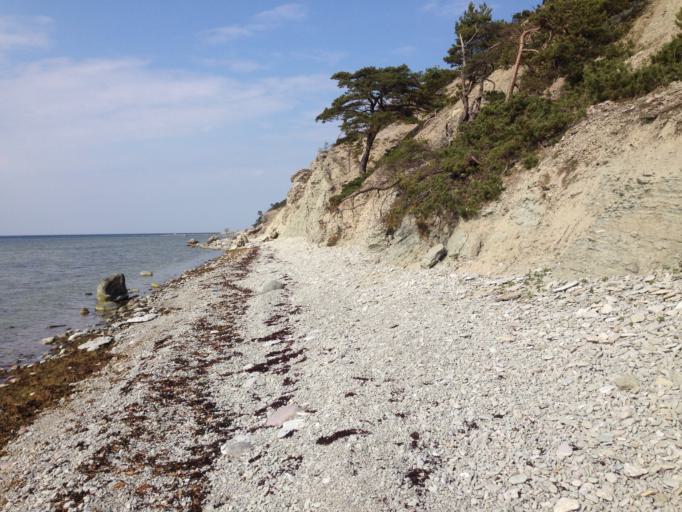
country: SE
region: Gotland
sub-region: Gotland
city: Slite
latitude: 57.8614
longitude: 18.6165
